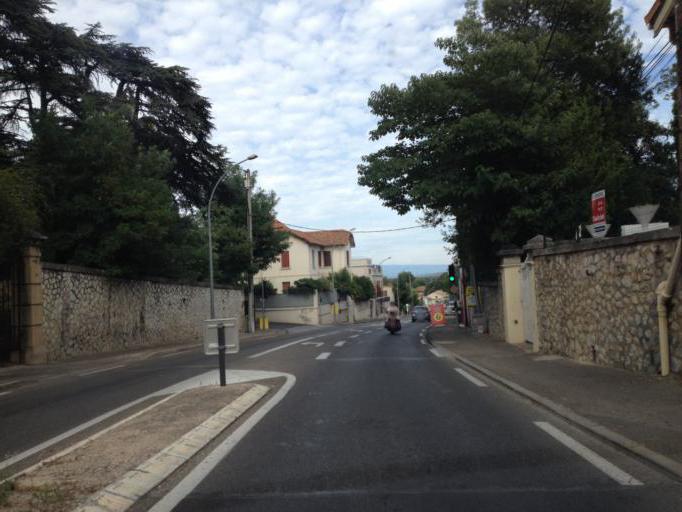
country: FR
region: Languedoc-Roussillon
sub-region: Departement du Gard
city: Villeneuve-les-Avignon
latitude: 43.9540
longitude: 4.7867
